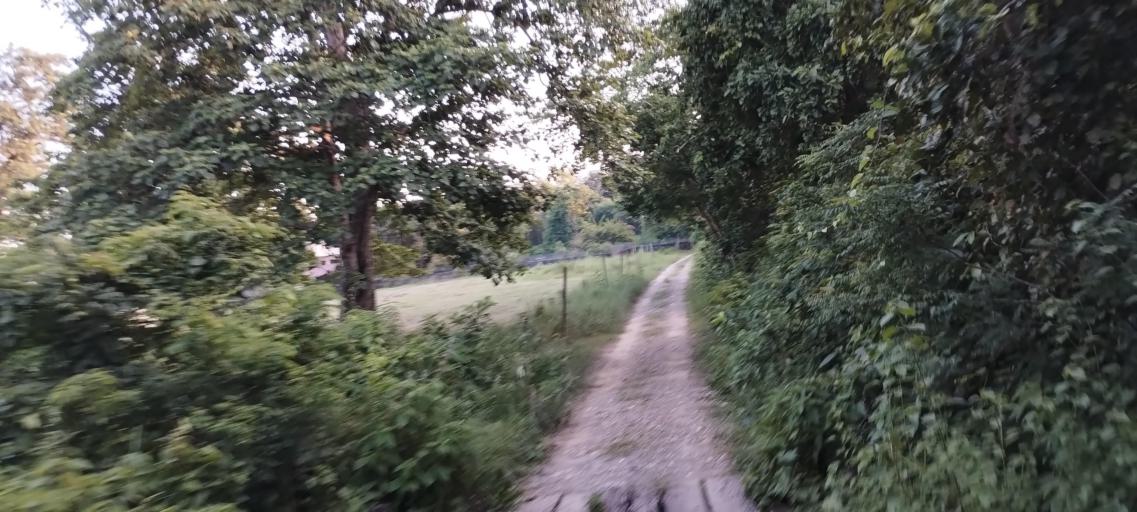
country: NP
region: Far Western
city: Tikapur
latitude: 28.4549
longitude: 81.2421
